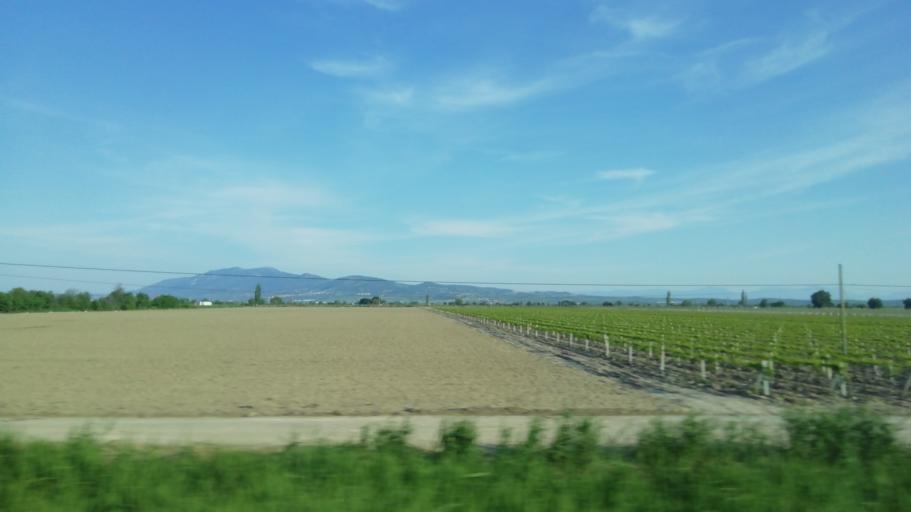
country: TR
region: Manisa
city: Saruhanli
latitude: 38.7430
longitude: 27.6074
